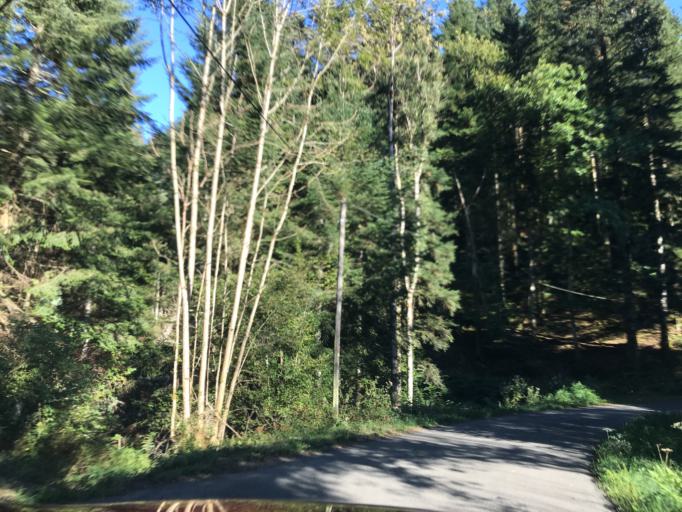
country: FR
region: Auvergne
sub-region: Departement du Puy-de-Dome
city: Escoutoux
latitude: 45.7767
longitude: 3.6156
